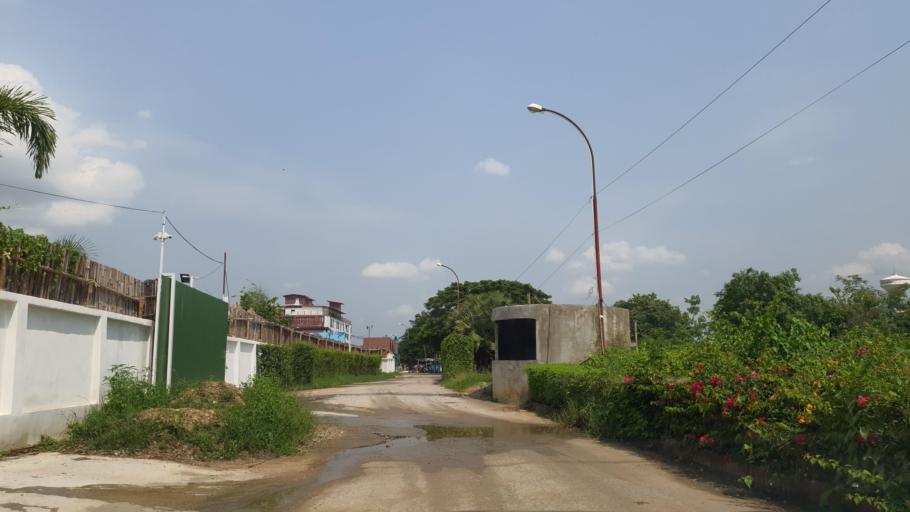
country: TH
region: Lamphun
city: Lamphun
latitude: 18.6021
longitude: 99.0144
